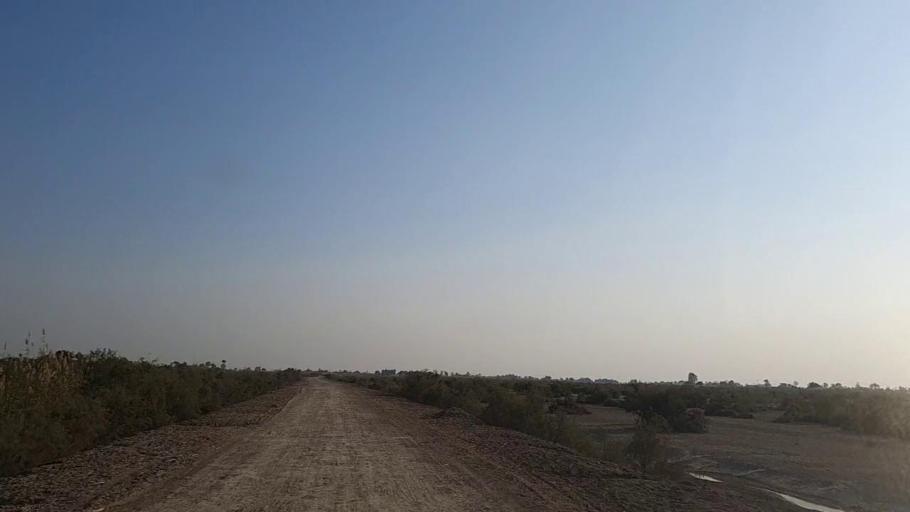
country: PK
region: Sindh
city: Daur
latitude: 26.4271
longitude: 68.3536
